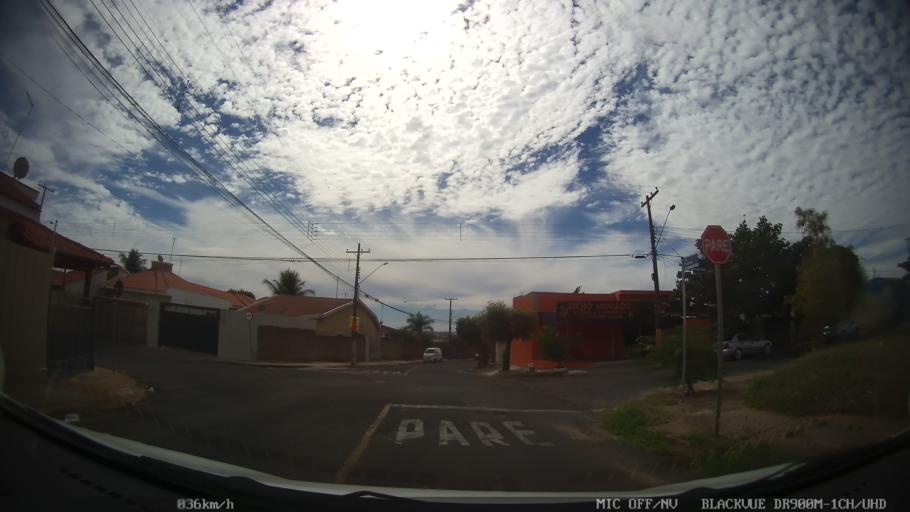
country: BR
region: Sao Paulo
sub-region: Catanduva
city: Catanduva
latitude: -21.1500
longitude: -48.9690
